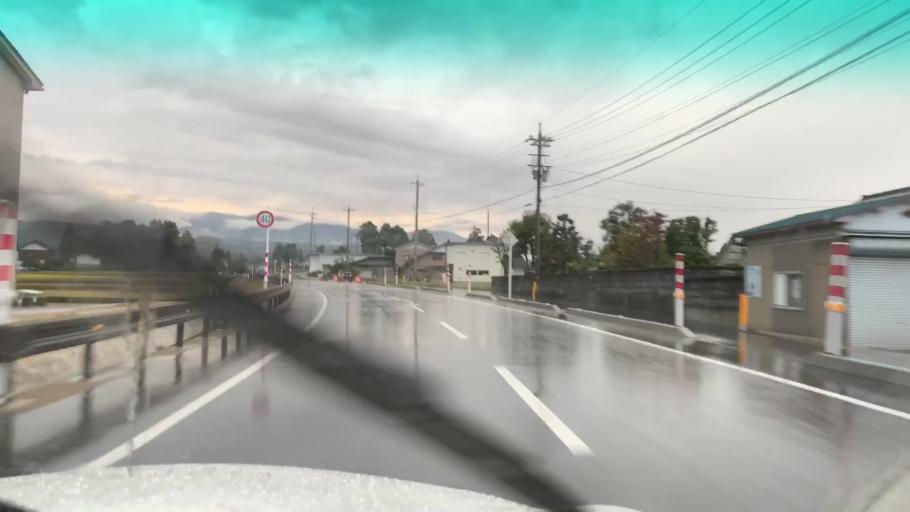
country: JP
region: Toyama
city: Kamiichi
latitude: 36.6469
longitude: 137.3279
